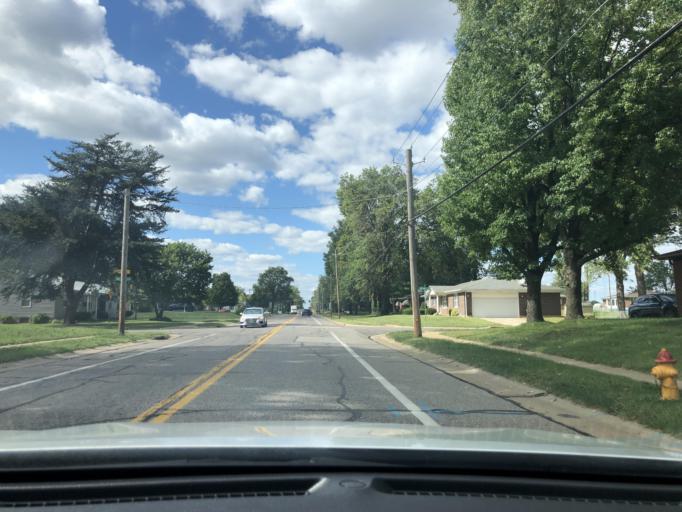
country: US
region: Missouri
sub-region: Saint Louis County
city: Concord
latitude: 38.4981
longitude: -90.3579
